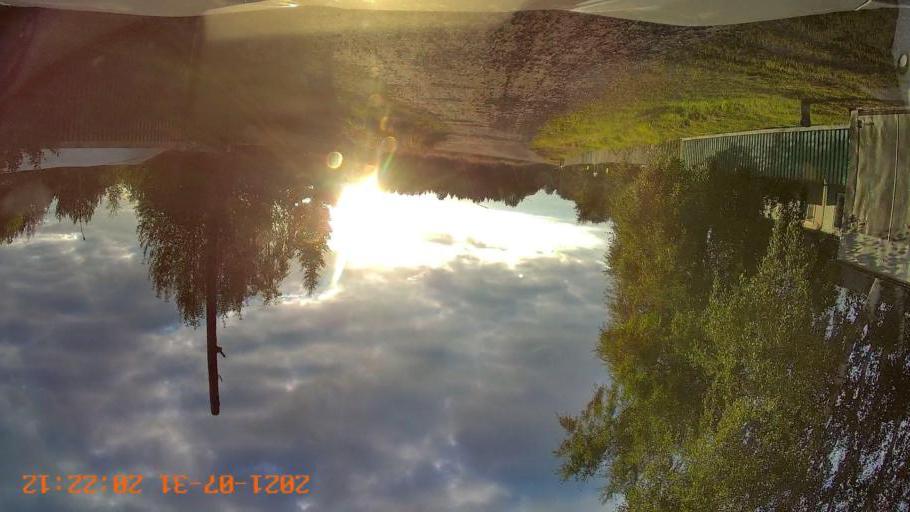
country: RU
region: Republic of Karelia
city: Pudozh
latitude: 61.6696
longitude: 36.3541
